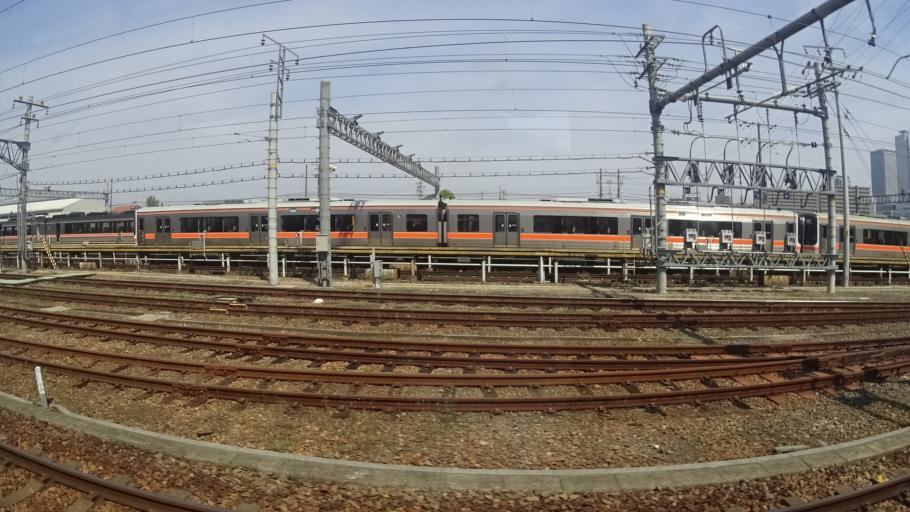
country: JP
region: Aichi
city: Nagoya-shi
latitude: 35.1599
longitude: 136.8788
